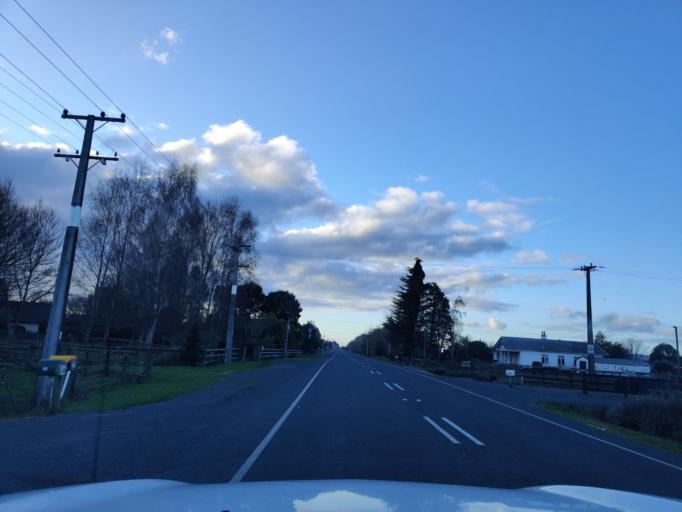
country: NZ
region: Waikato
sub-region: Waipa District
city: Cambridge
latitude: -37.8836
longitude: 175.4389
